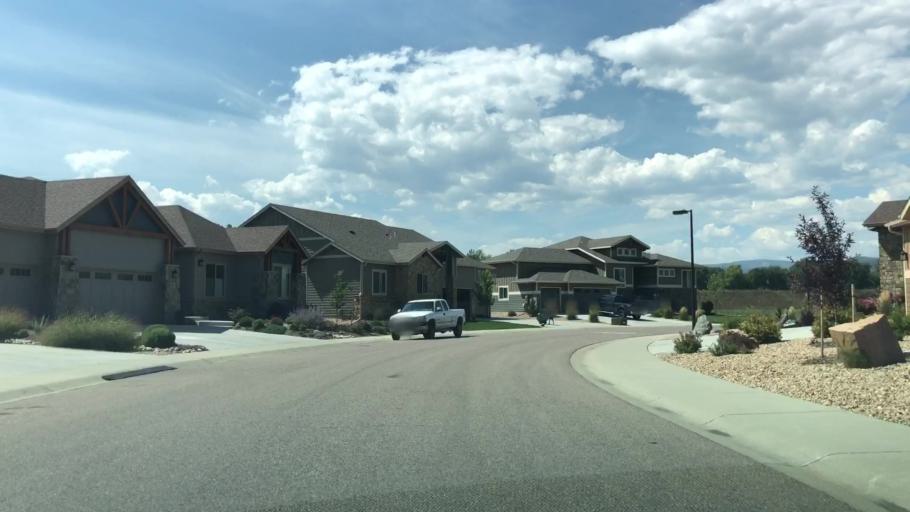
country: US
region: Colorado
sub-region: Larimer County
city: Loveland
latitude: 40.3947
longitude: -105.1570
